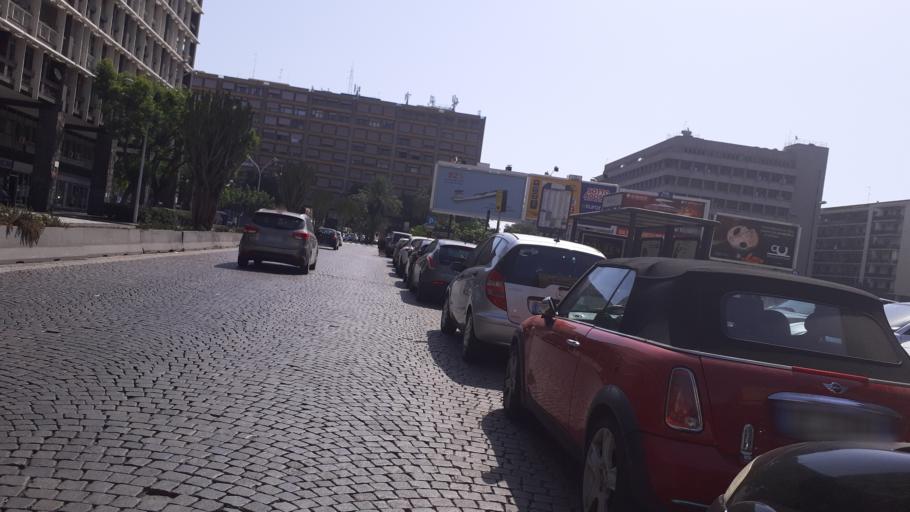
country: IT
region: Sicily
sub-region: Catania
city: Catania
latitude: 37.5076
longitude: 15.0903
